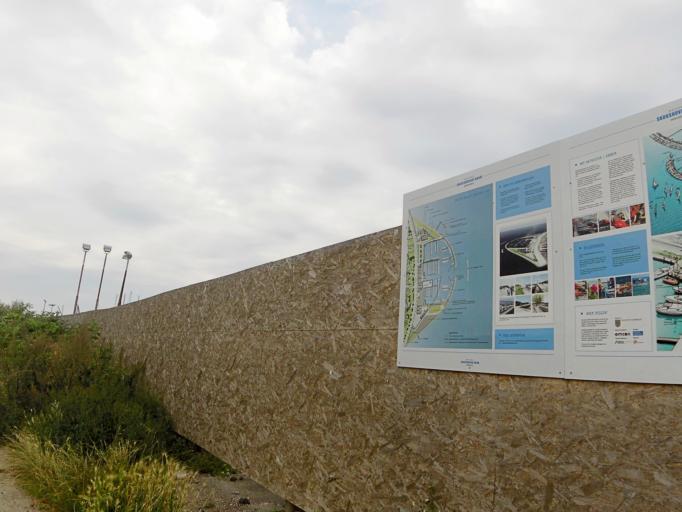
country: DK
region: Capital Region
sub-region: Gentofte Kommune
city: Charlottenlund
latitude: 55.7578
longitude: 12.5981
